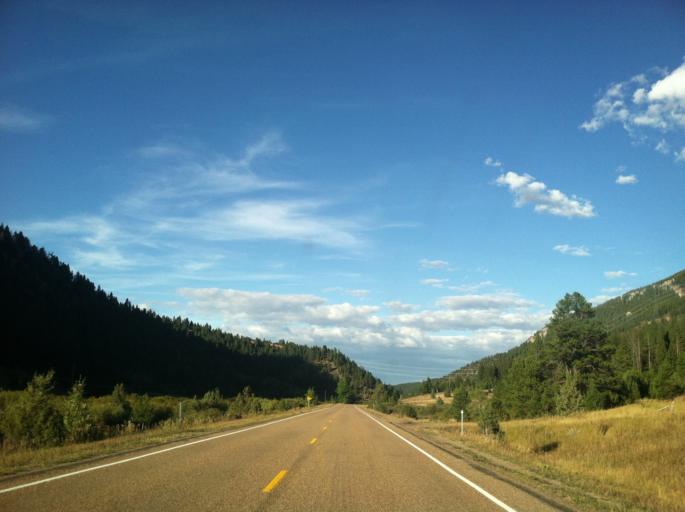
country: US
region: Montana
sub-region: Granite County
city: Philipsburg
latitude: 46.4352
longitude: -113.2669
